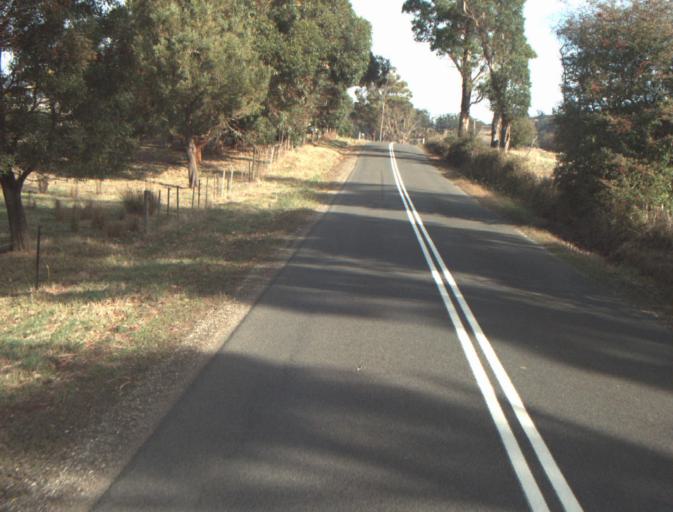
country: AU
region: Tasmania
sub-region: Launceston
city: Mayfield
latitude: -41.2270
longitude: 147.1228
